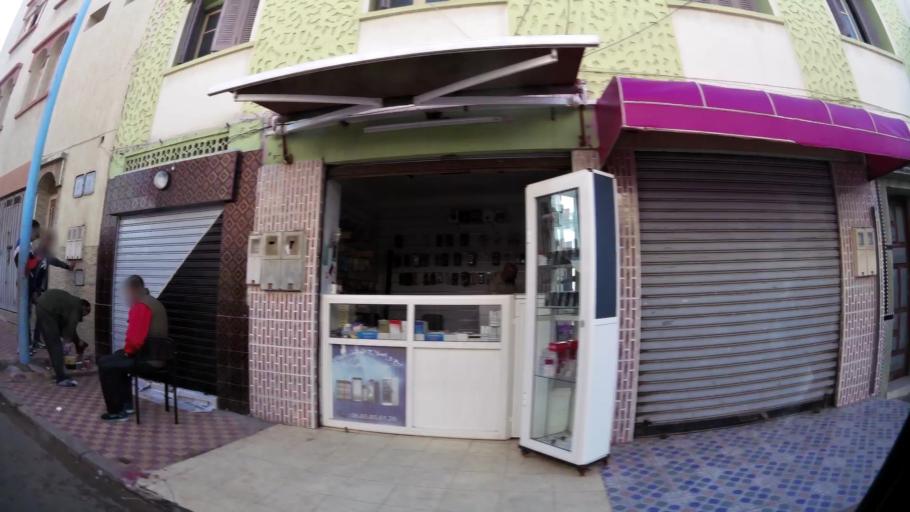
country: MA
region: Doukkala-Abda
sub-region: El-Jadida
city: El Jadida
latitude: 33.2431
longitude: -8.5268
